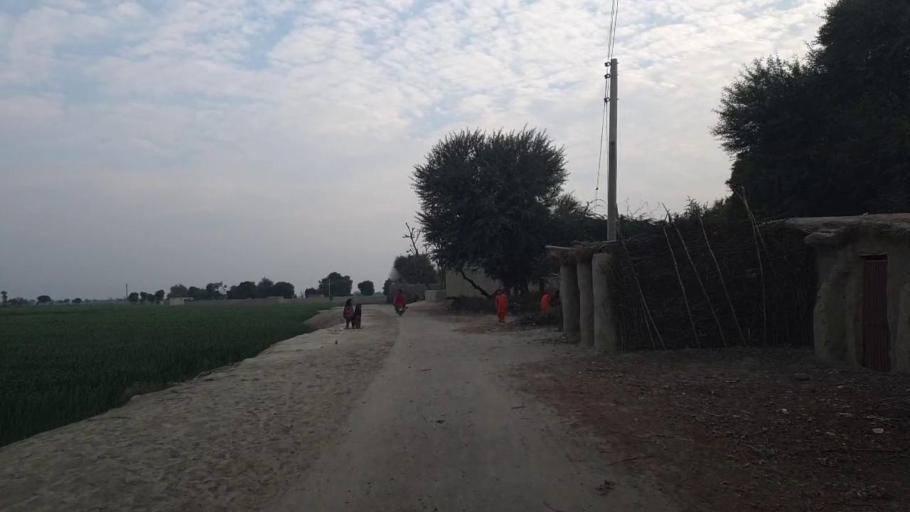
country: PK
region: Sindh
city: Shahpur Chakar
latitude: 26.0886
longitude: 68.5383
